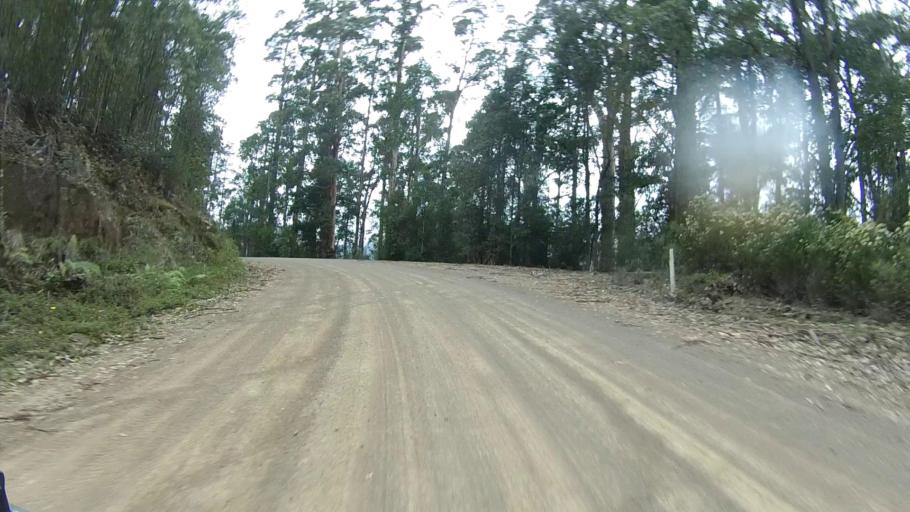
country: AU
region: Tasmania
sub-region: Sorell
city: Sorell
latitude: -42.6998
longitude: 147.8550
